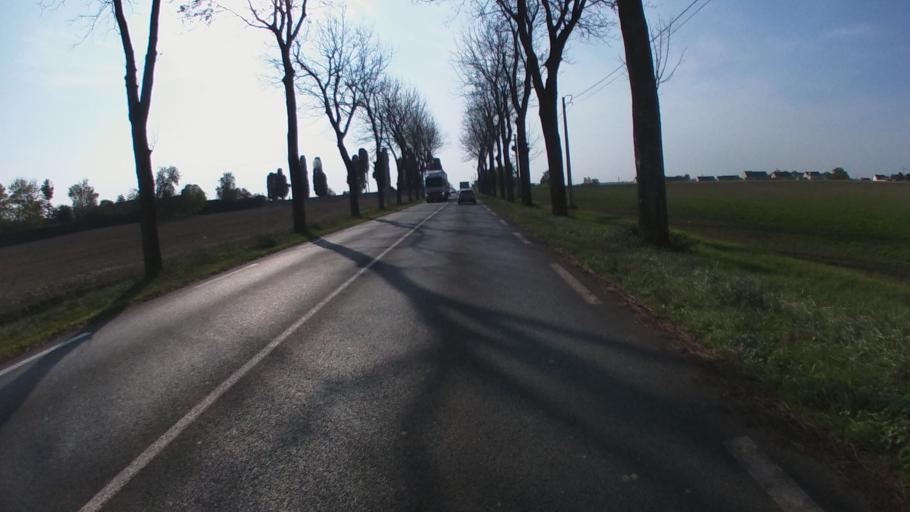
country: FR
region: Pays de la Loire
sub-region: Departement de Maine-et-Loire
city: Distre
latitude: 47.1976
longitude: -0.1245
